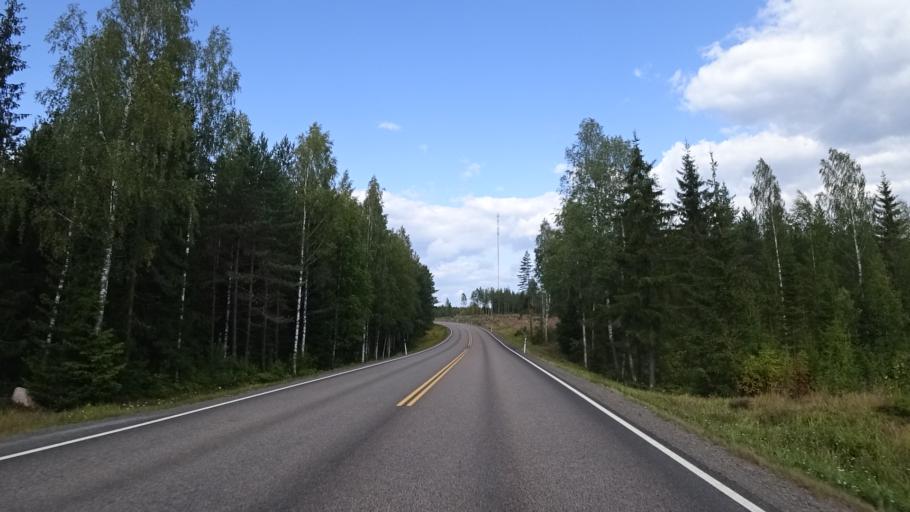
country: FI
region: Kymenlaakso
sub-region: Kotka-Hamina
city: Hamina
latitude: 60.7285
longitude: 27.3261
